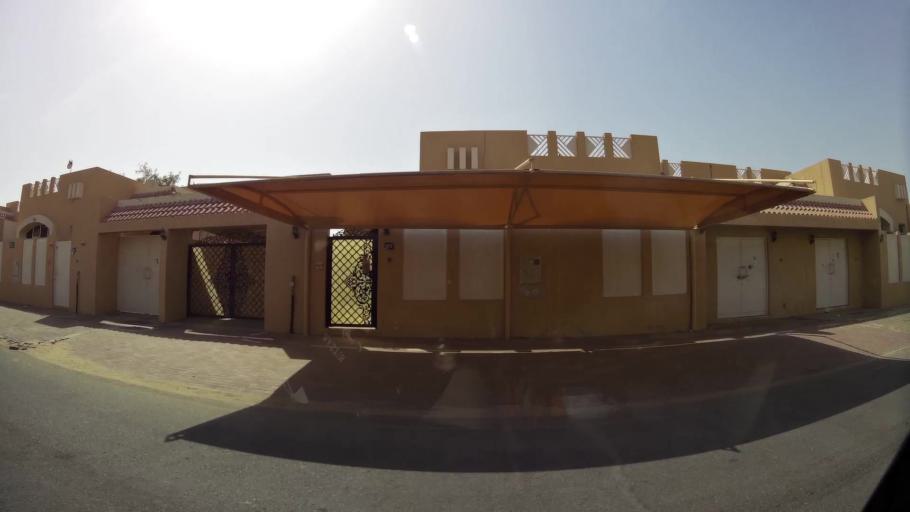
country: AE
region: Dubai
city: Dubai
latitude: 25.1622
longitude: 55.2539
